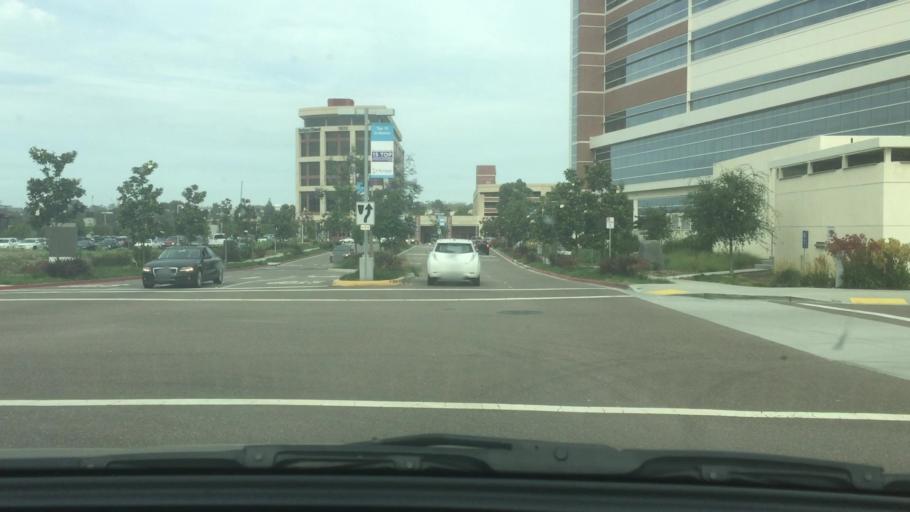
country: US
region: California
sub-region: San Diego County
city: La Jolla
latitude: 32.8840
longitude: -117.2234
